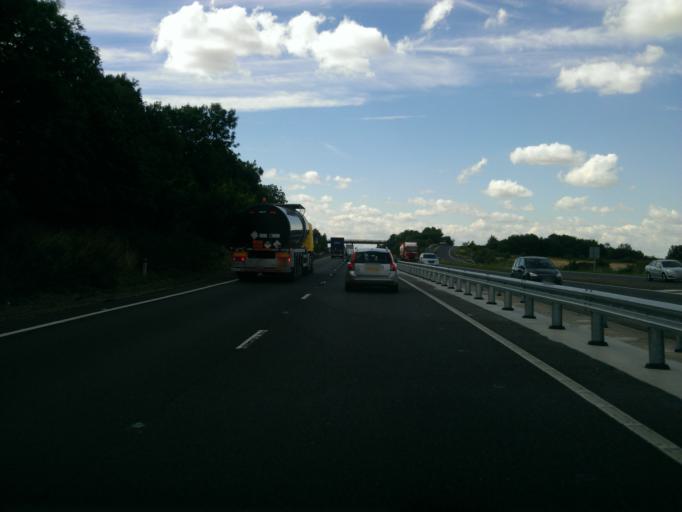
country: GB
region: England
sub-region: Bedford
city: Pertenhall
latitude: 52.3440
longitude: -0.3435
